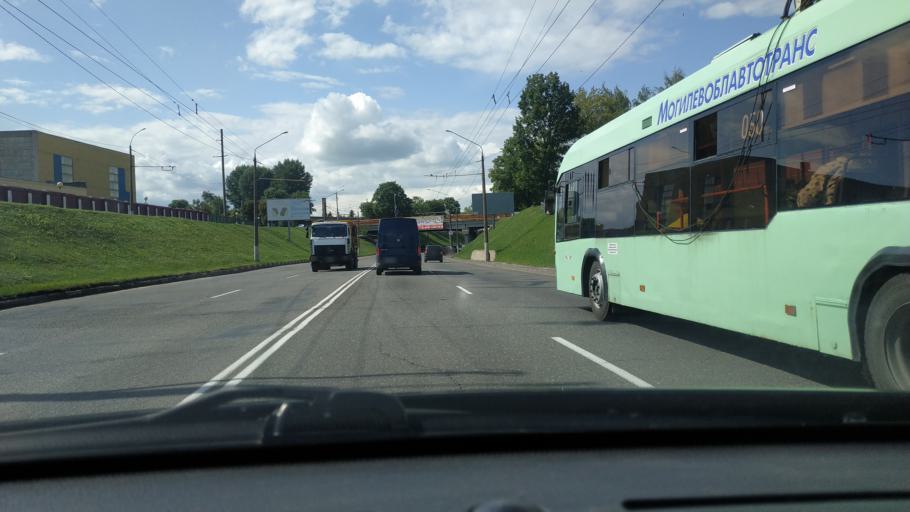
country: BY
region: Mogilev
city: Mahilyow
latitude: 53.8911
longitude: 30.3019
